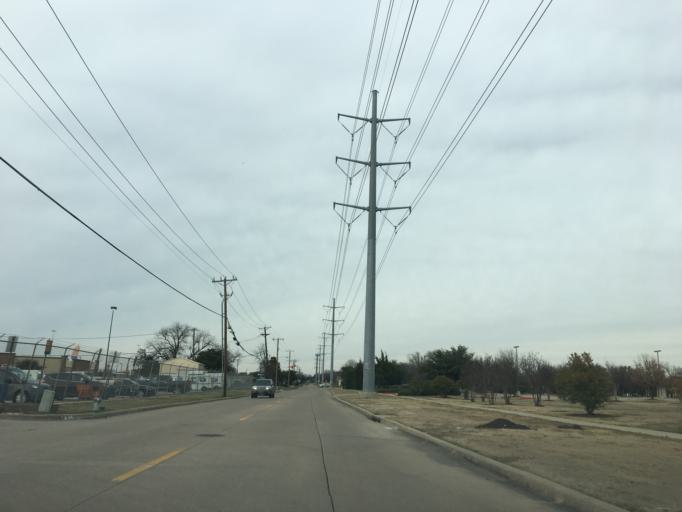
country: US
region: Texas
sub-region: Collin County
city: McKinney
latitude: 33.2016
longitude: -96.6364
